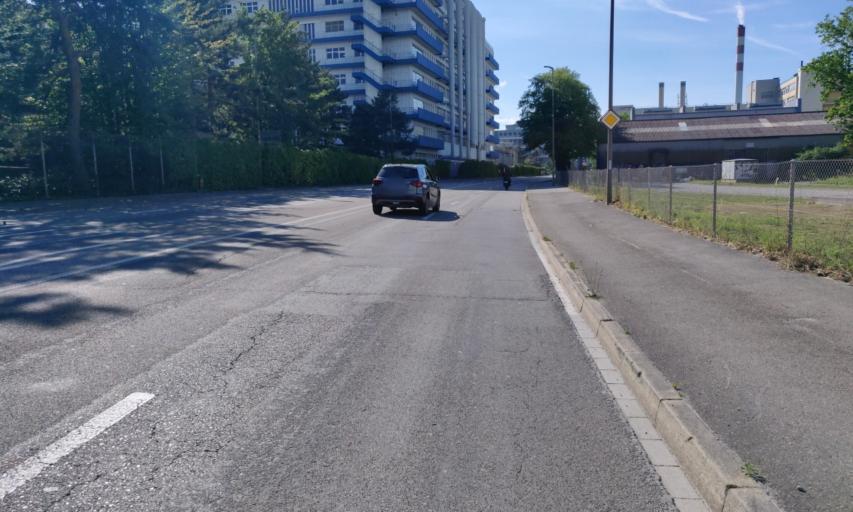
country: DE
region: Baden-Wuerttemberg
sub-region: Freiburg Region
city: Grenzach-Wyhlen
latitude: 47.5327
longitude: 7.6699
